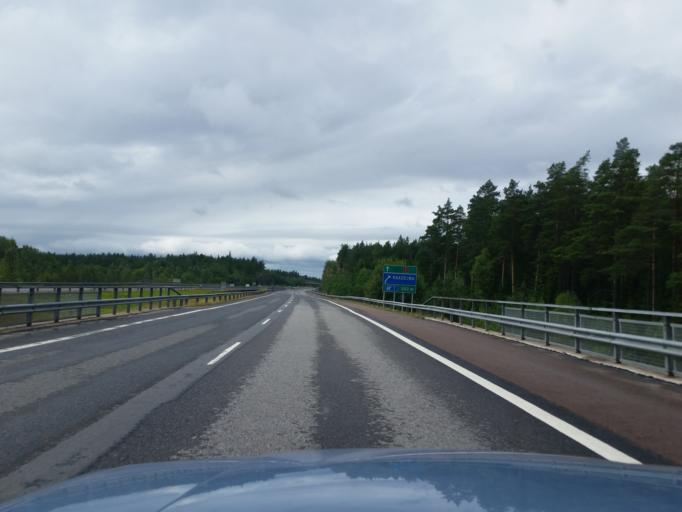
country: FI
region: Varsinais-Suomi
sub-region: Turku
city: Piikkioe
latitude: 60.4367
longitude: 22.4615
